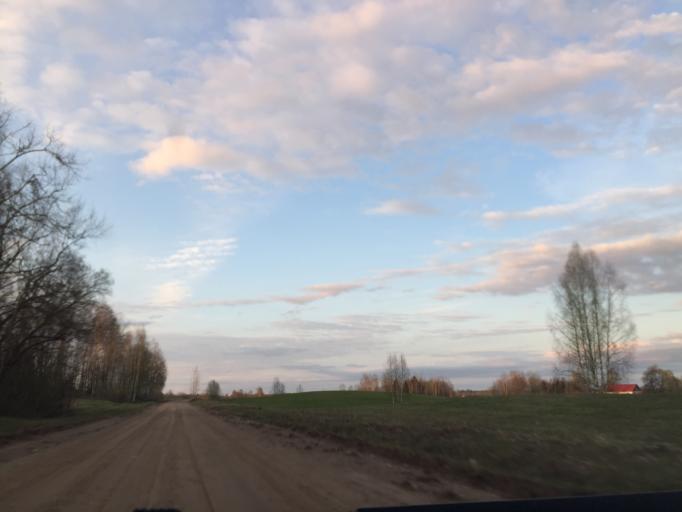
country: LV
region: Gulbenes Rajons
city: Gulbene
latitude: 57.2314
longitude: 26.8020
